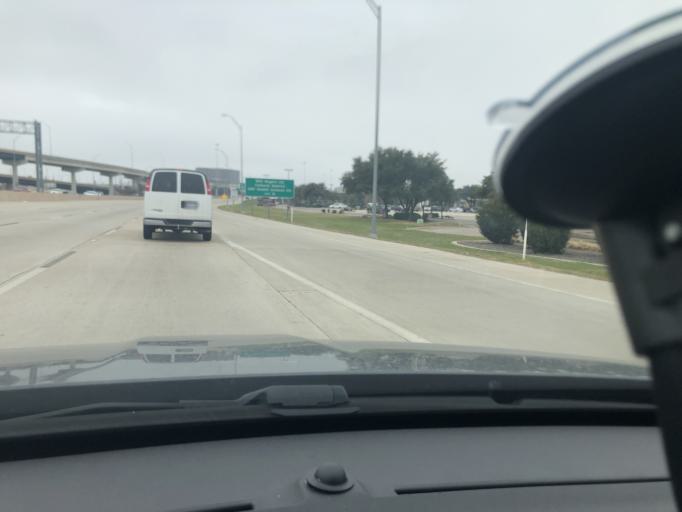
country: US
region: Texas
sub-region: Tarrant County
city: Fort Worth
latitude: 32.7360
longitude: -97.3561
